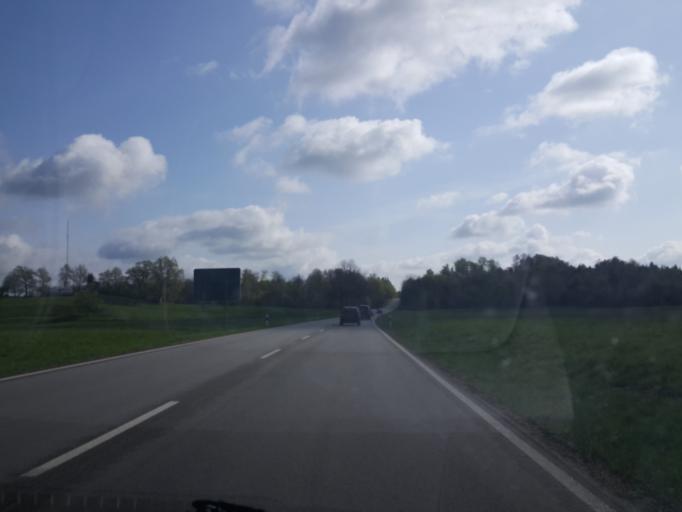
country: DE
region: Bavaria
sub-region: Upper Bavaria
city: Reichersbeuern
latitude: 47.7670
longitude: 11.6443
